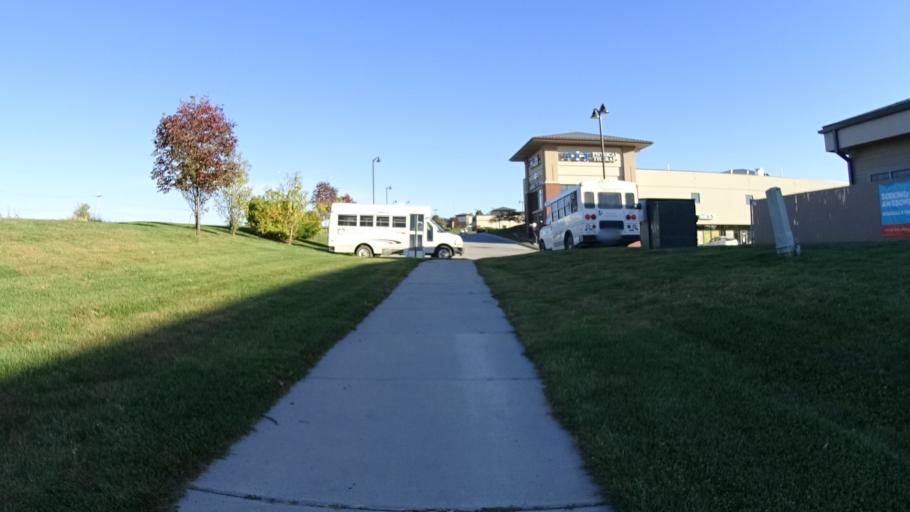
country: US
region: Nebraska
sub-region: Sarpy County
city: Papillion
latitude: 41.1458
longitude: -96.0660
